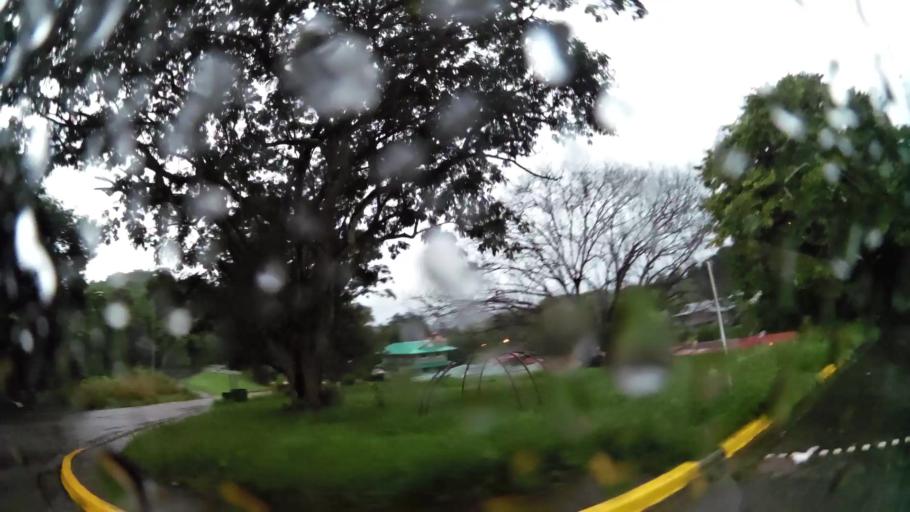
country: PA
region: Panama
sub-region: Distrito de Panama
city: Paraiso
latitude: 9.0328
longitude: -79.6253
